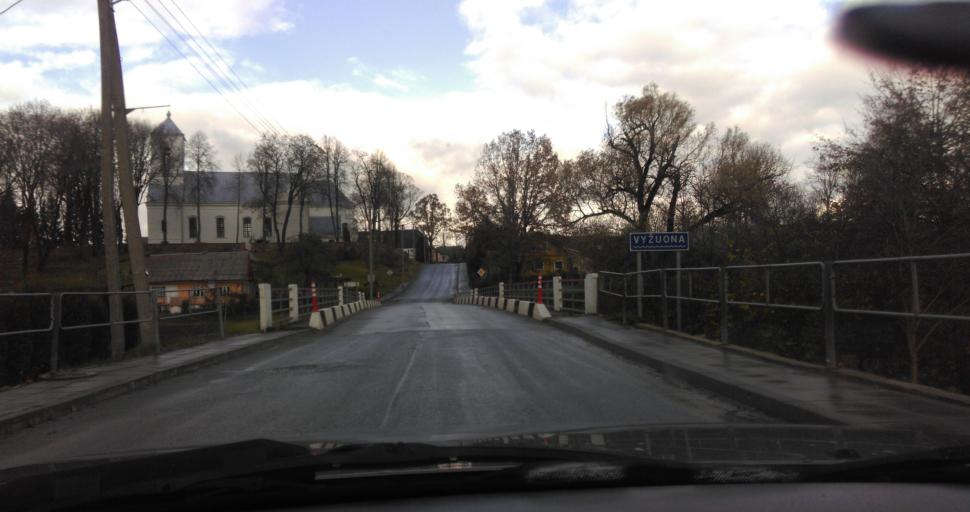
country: LT
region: Utenos apskritis
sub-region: Utena
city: Utena
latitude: 55.5841
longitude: 25.4949
